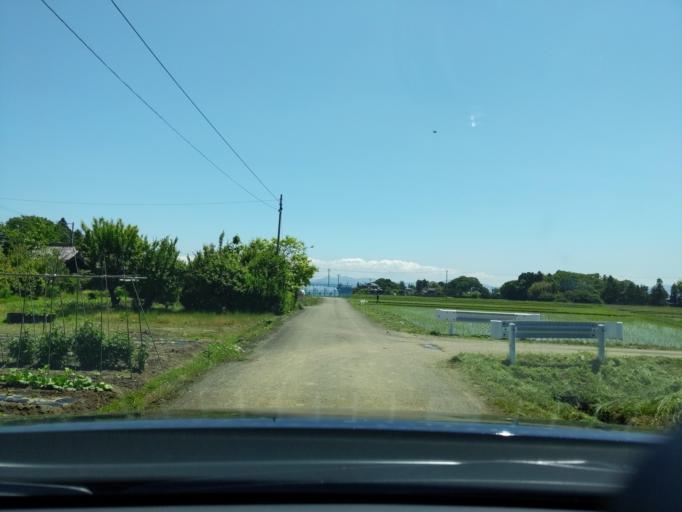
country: JP
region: Fukushima
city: Koriyama
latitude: 37.3874
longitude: 140.2918
